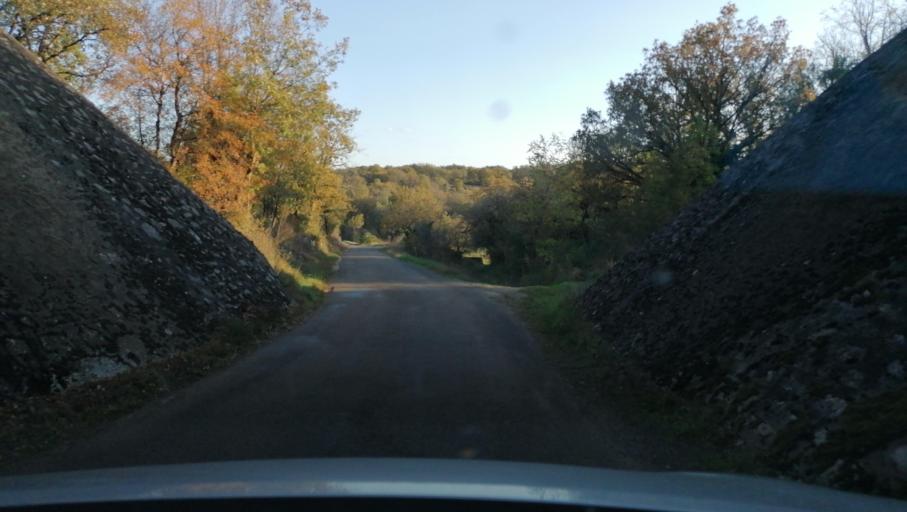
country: FR
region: Midi-Pyrenees
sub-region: Departement du Lot
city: Vayrac
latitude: 44.8799
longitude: 1.6547
